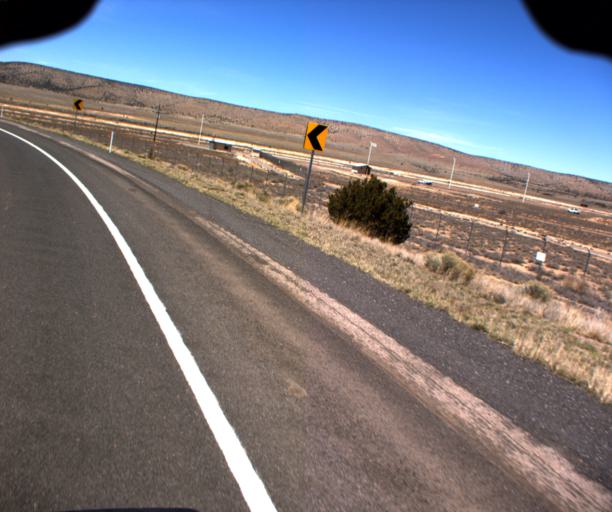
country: US
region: Arizona
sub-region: Mohave County
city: Peach Springs
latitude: 35.3310
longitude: -112.8867
